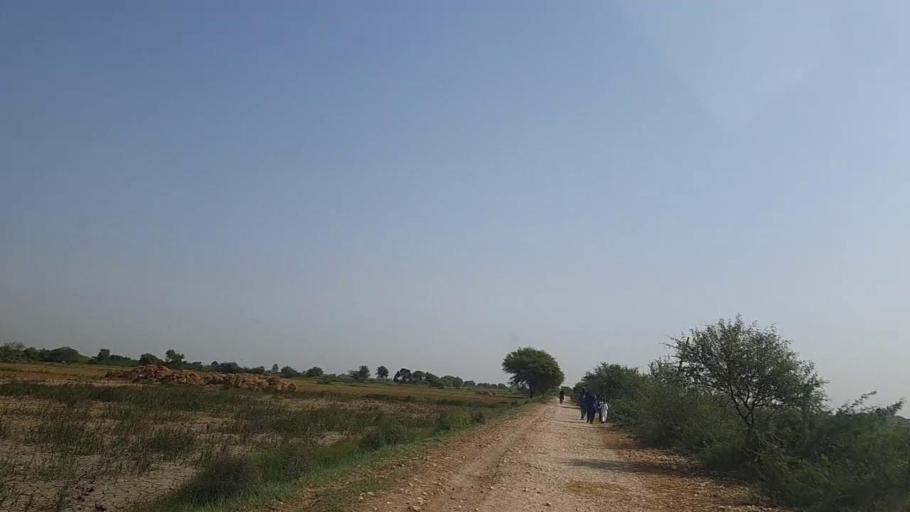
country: PK
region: Sindh
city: Daro Mehar
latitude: 24.7206
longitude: 68.0902
